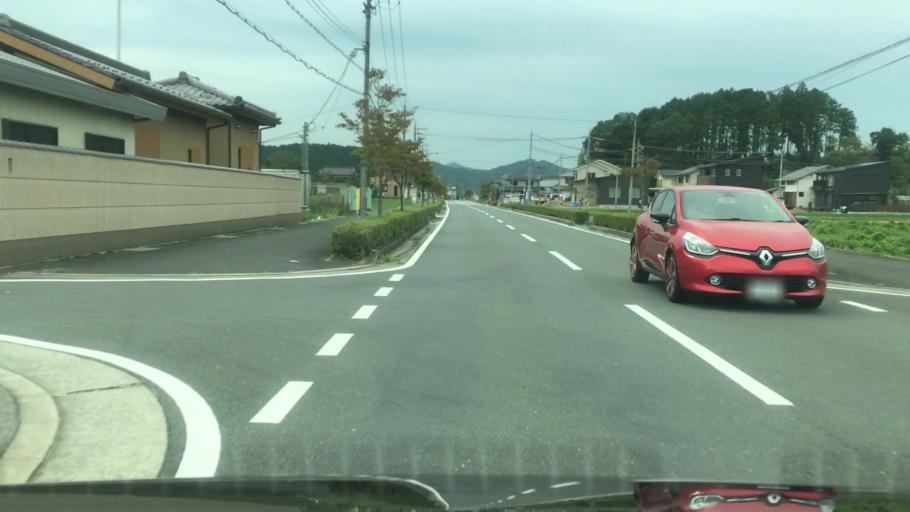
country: JP
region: Hyogo
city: Sasayama
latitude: 35.0723
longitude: 135.1920
